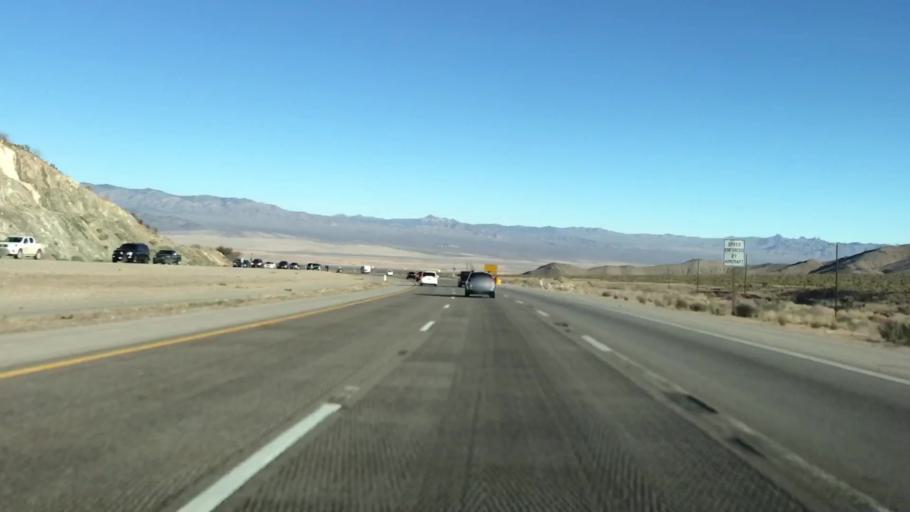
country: US
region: Nevada
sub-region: Clark County
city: Sandy Valley
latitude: 35.4609
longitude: -115.4714
